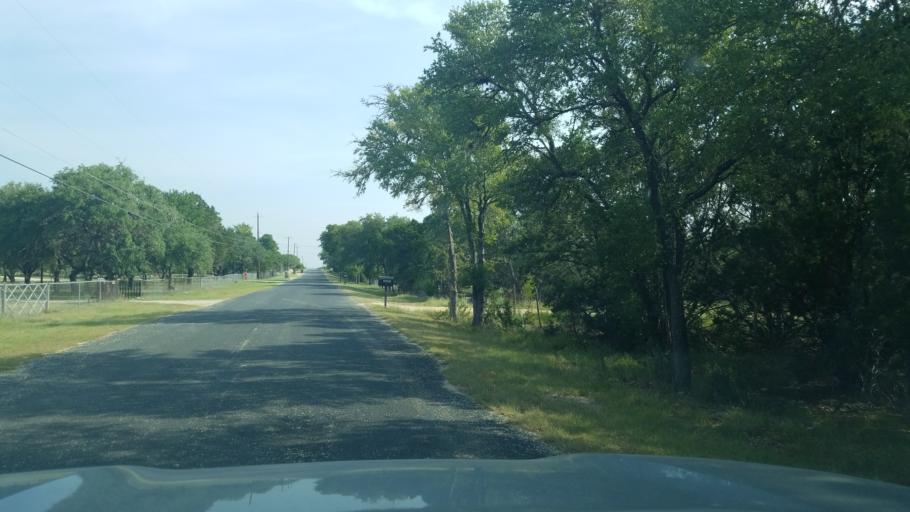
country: US
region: Texas
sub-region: Bexar County
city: Timberwood Park
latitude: 29.7198
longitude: -98.4887
